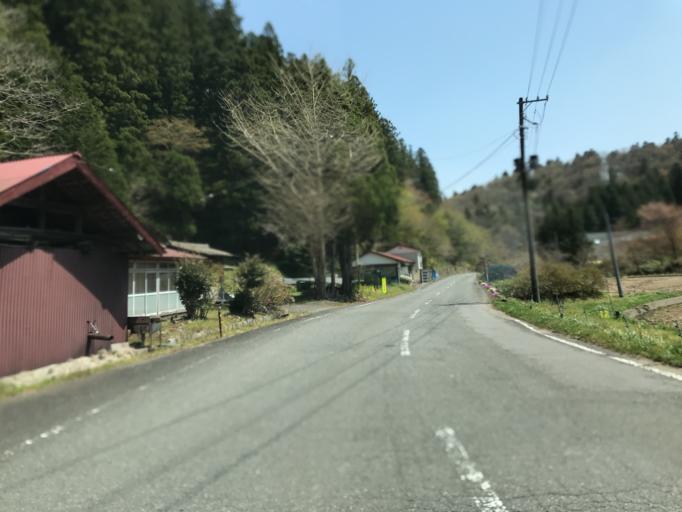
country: JP
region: Ibaraki
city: Kitaibaraki
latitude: 36.9659
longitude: 140.6617
